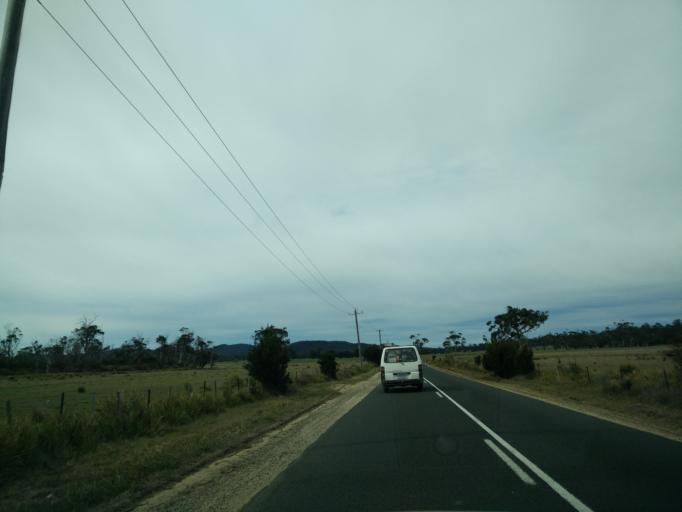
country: AU
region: Tasmania
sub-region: Break O'Day
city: St Helens
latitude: -41.9001
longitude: 148.2549
